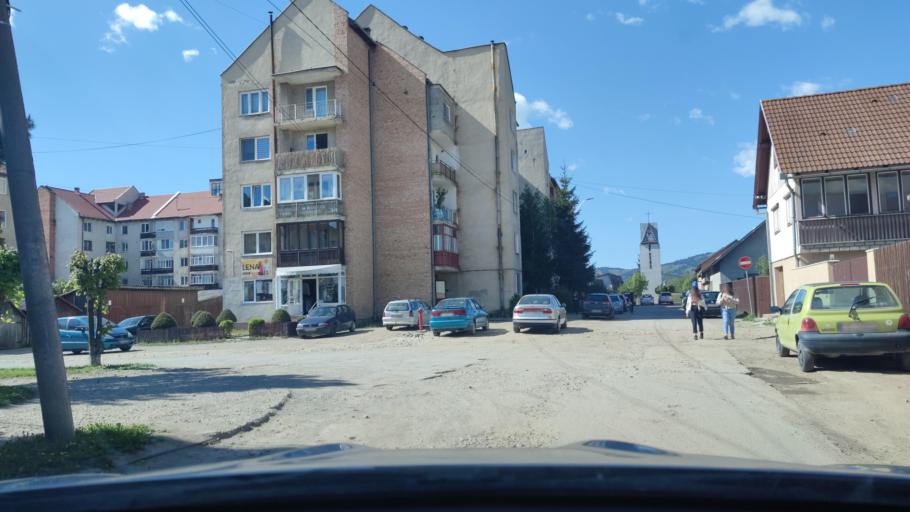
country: RO
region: Harghita
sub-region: Municipiul Gheorgheni
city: Gheorgheni
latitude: 46.7206
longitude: 25.5896
